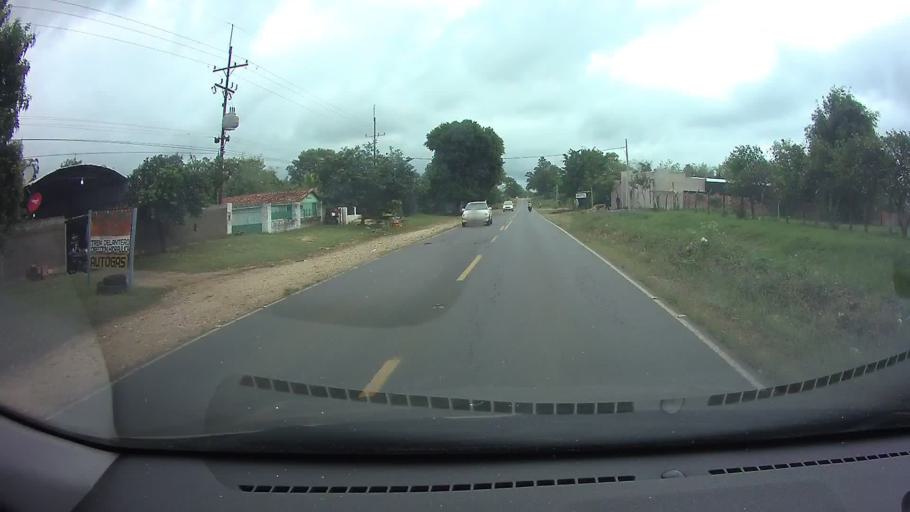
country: PY
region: Central
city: Guarambare
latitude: -25.5025
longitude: -57.4820
